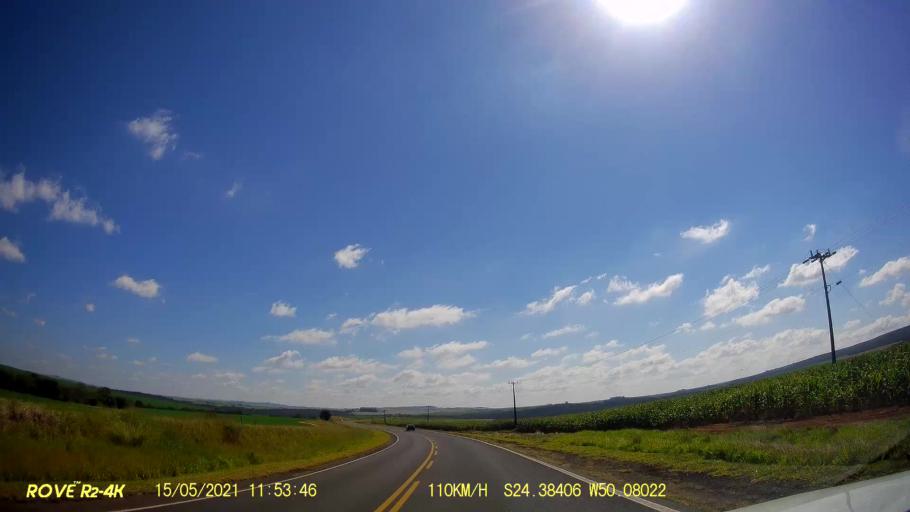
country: BR
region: Parana
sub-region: Pirai Do Sul
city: Pirai do Sul
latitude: -24.3848
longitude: -50.0798
